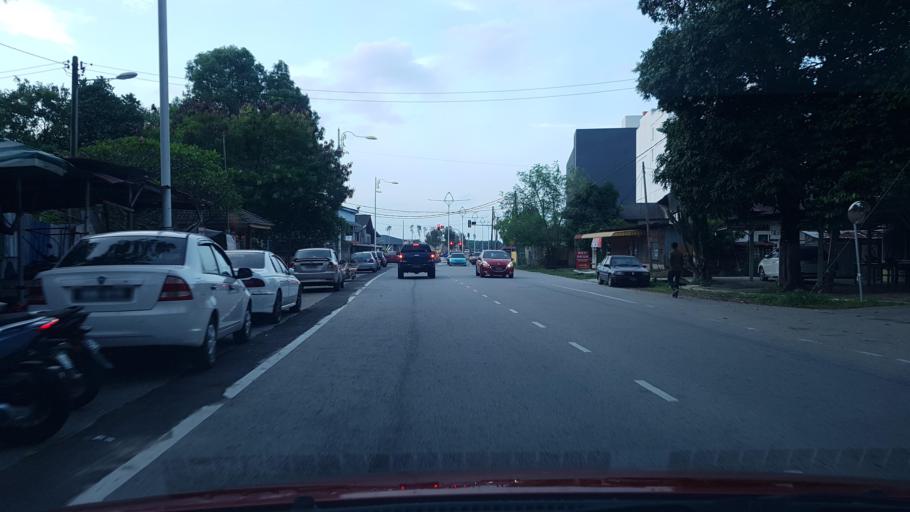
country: MY
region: Terengganu
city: Kuala Terengganu
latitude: 5.3351
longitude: 103.1425
